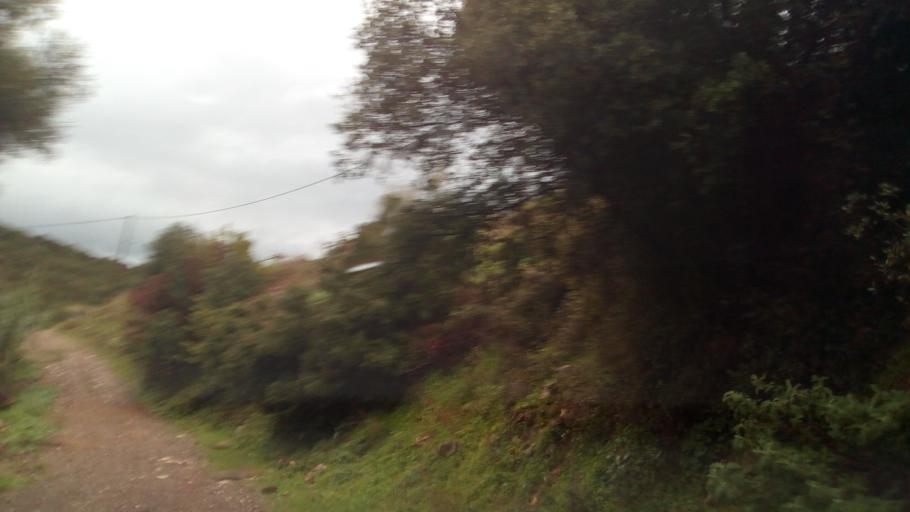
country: GR
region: West Greece
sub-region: Nomos Aitolias kai Akarnanias
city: Nafpaktos
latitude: 38.4157
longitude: 21.9031
